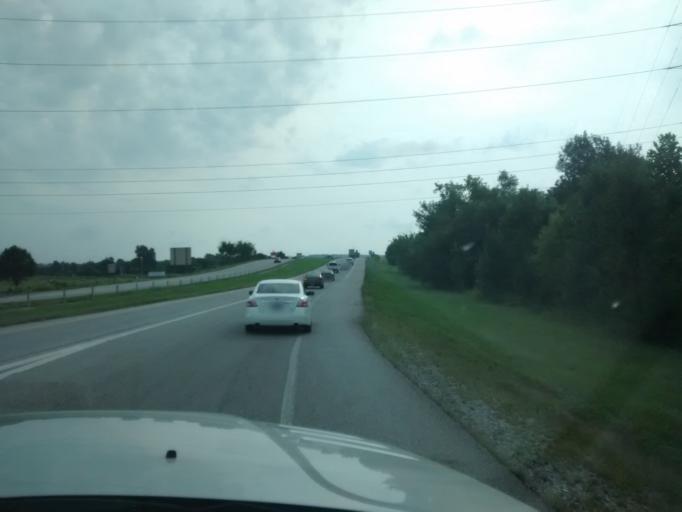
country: US
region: Arkansas
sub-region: Washington County
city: Johnson
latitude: 36.1099
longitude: -94.1676
